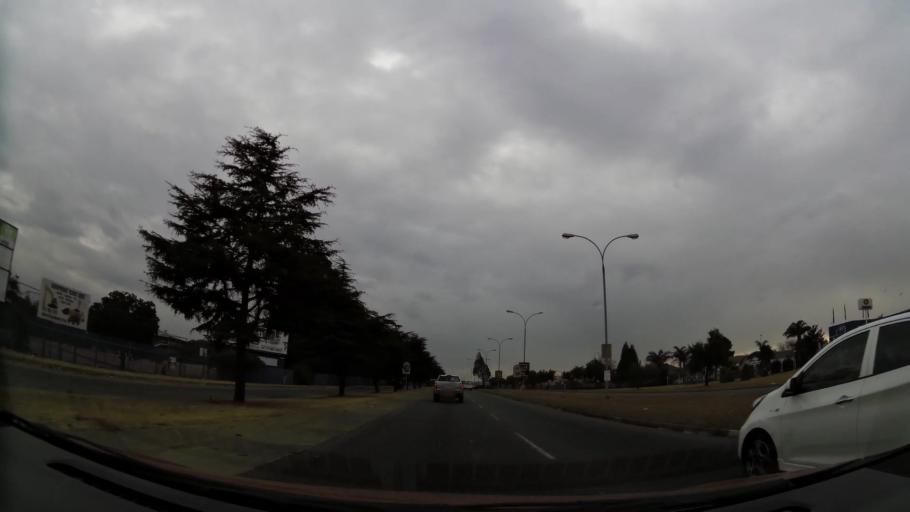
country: ZA
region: Gauteng
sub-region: City of Johannesburg Metropolitan Municipality
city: Roodepoort
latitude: -26.1432
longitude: 27.8752
